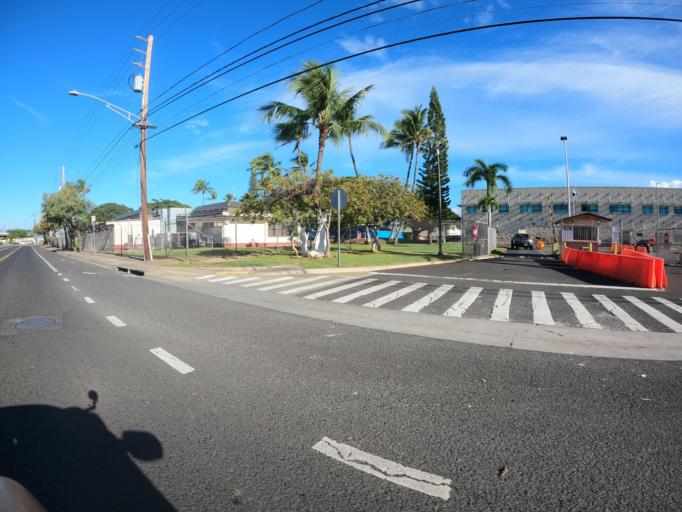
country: US
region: Hawaii
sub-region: Honolulu County
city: Honolulu
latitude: 21.3057
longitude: -157.8742
